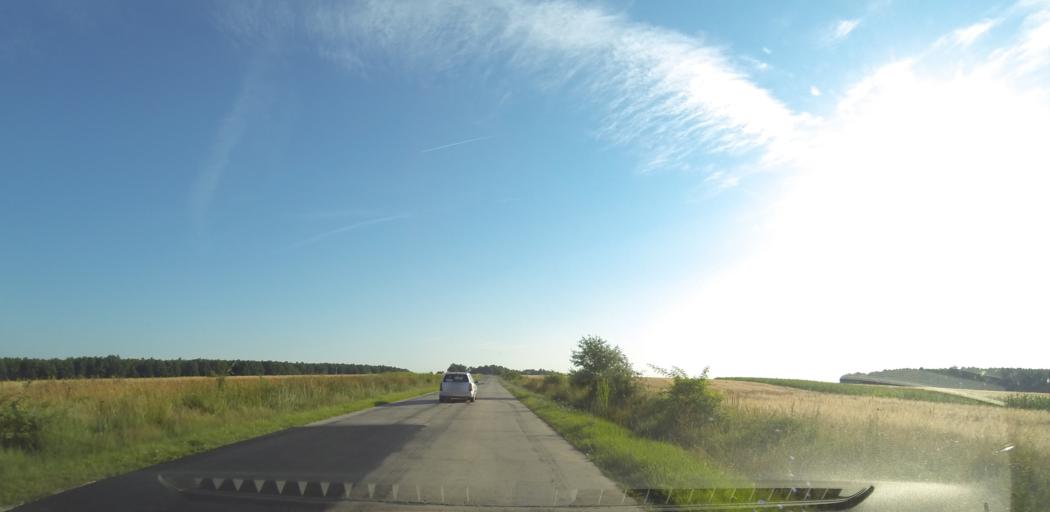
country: RO
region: Valcea
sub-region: Comuna Balcesti
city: Balcesti
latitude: 44.6005
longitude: 23.9283
